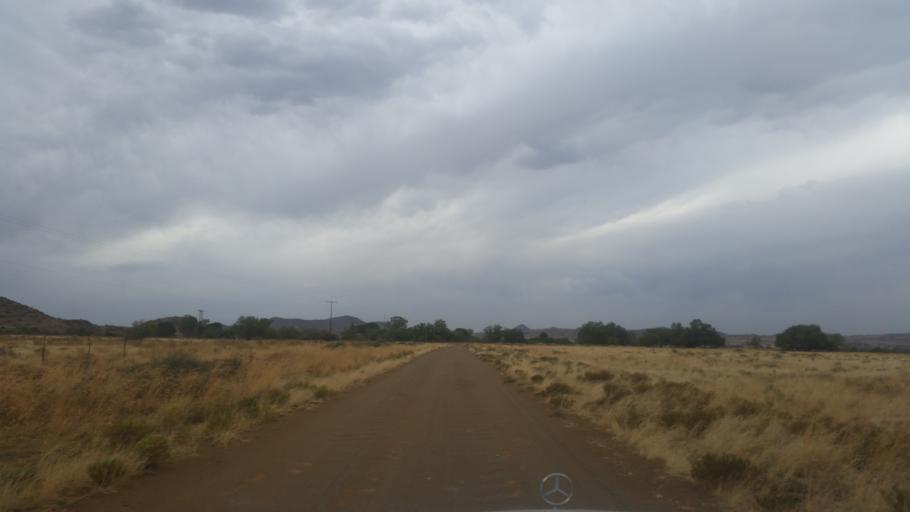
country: ZA
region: Orange Free State
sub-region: Xhariep District Municipality
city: Trompsburg
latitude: -30.5011
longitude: 25.9553
